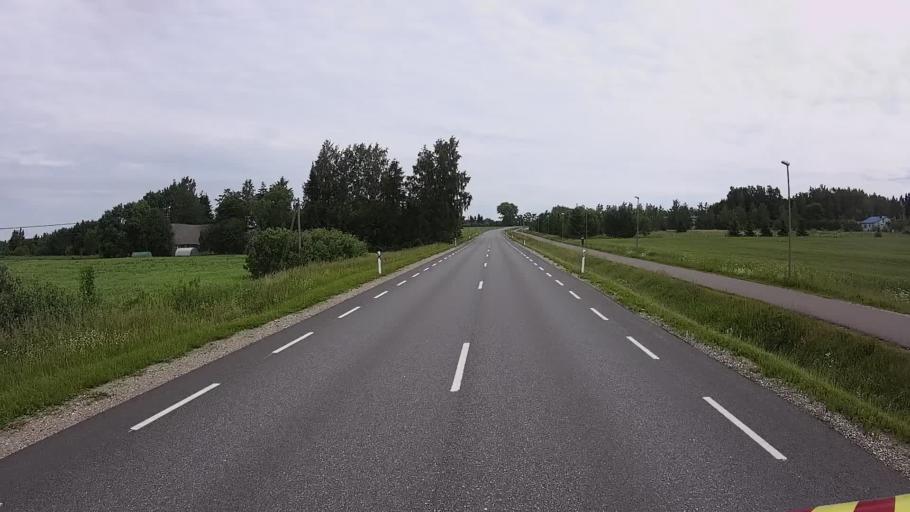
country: EE
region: Viljandimaa
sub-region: Karksi vald
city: Karksi-Nuia
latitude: 58.1129
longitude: 25.5719
